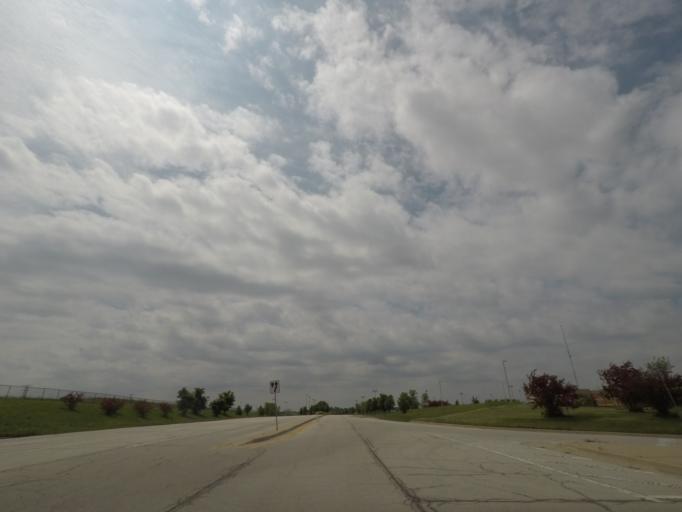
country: US
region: Illinois
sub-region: Winnebago County
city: Machesney Park
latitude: 42.3264
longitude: -88.9503
